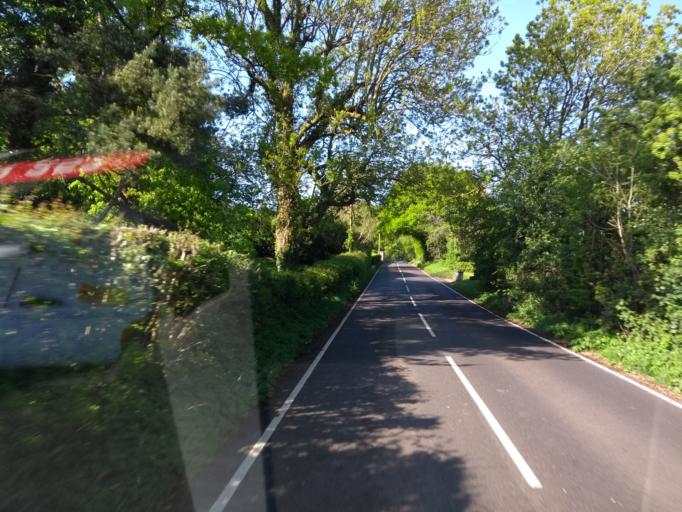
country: GB
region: England
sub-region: Somerset
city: Taunton
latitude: 50.9488
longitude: -3.0907
